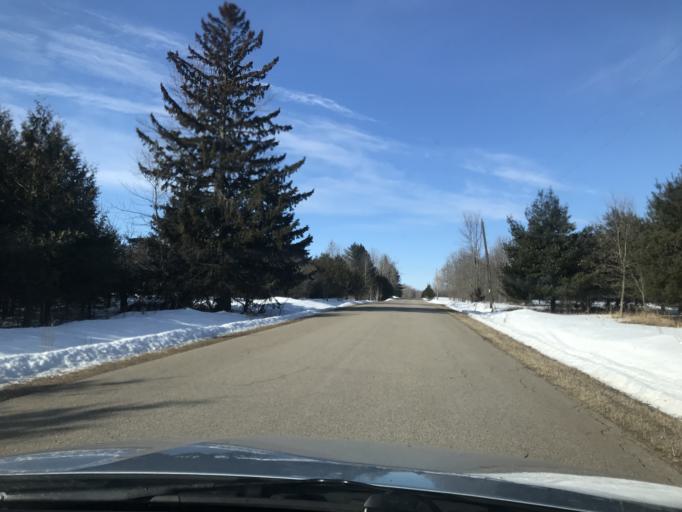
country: US
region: Wisconsin
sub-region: Oconto County
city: Oconto Falls
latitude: 44.9232
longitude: -88.1715
